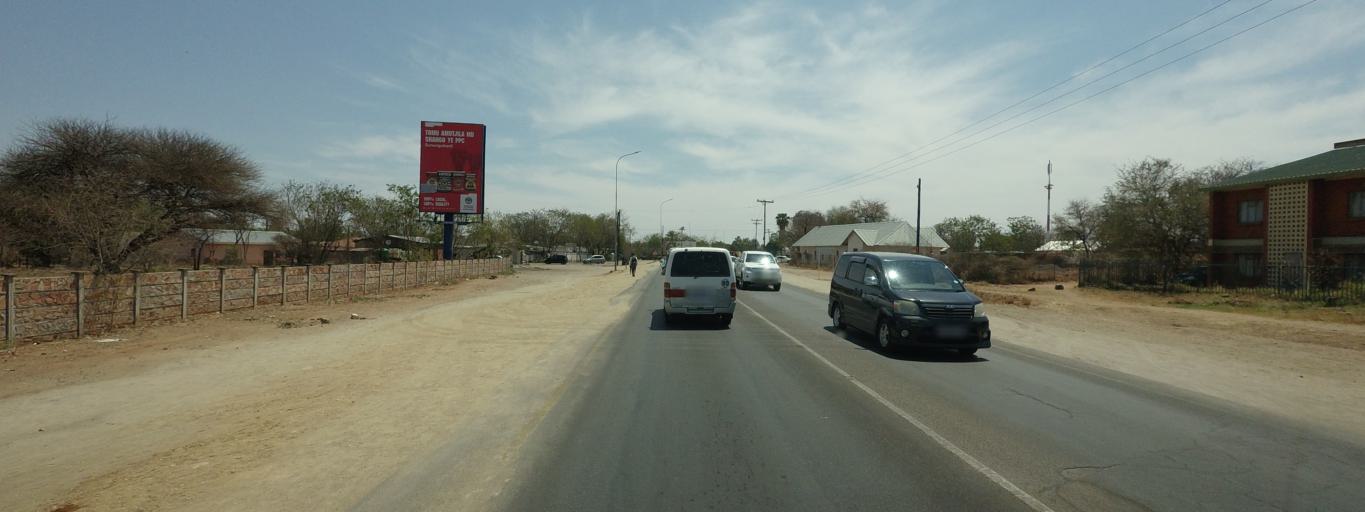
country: BW
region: North East
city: Francistown
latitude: -21.1720
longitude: 27.5051
